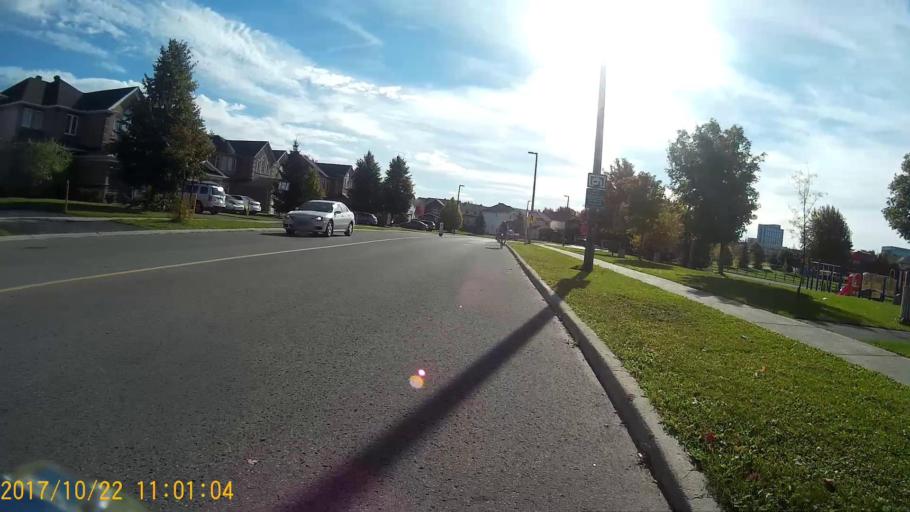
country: CA
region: Ontario
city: Bells Corners
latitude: 45.3555
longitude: -75.9201
